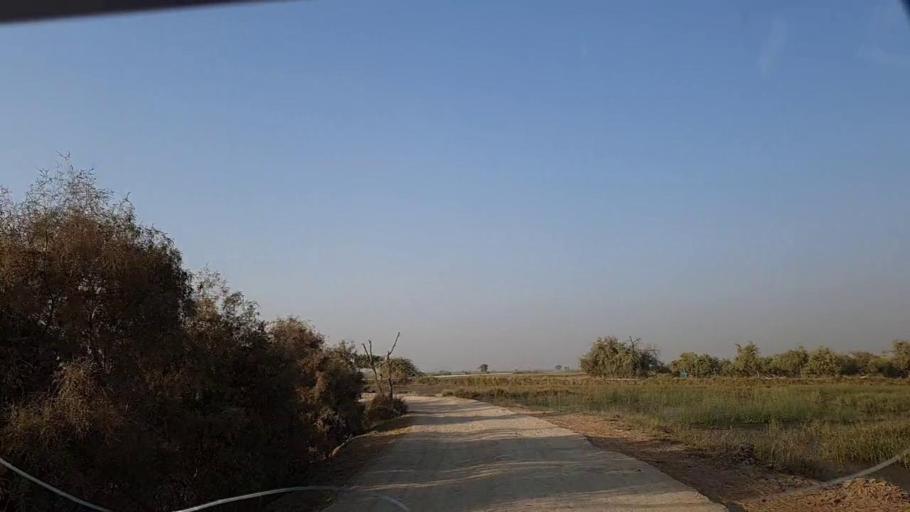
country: PK
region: Sindh
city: Rustam jo Goth
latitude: 27.9744
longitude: 68.8054
